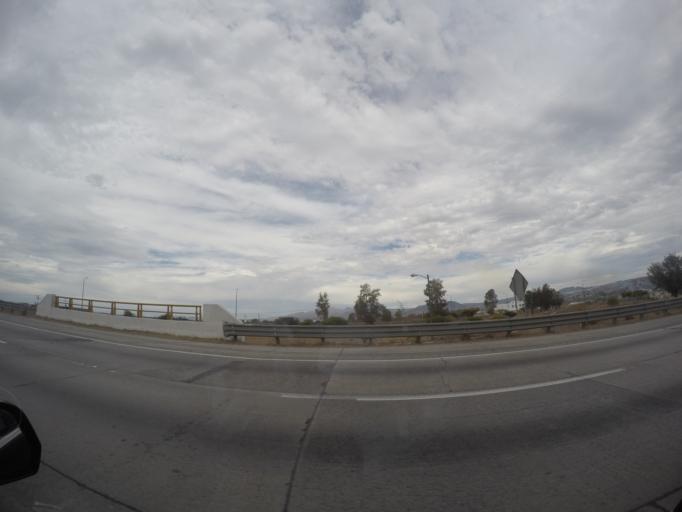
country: MX
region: Queretaro
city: San Juan del Rio
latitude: 20.3933
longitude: -100.0217
